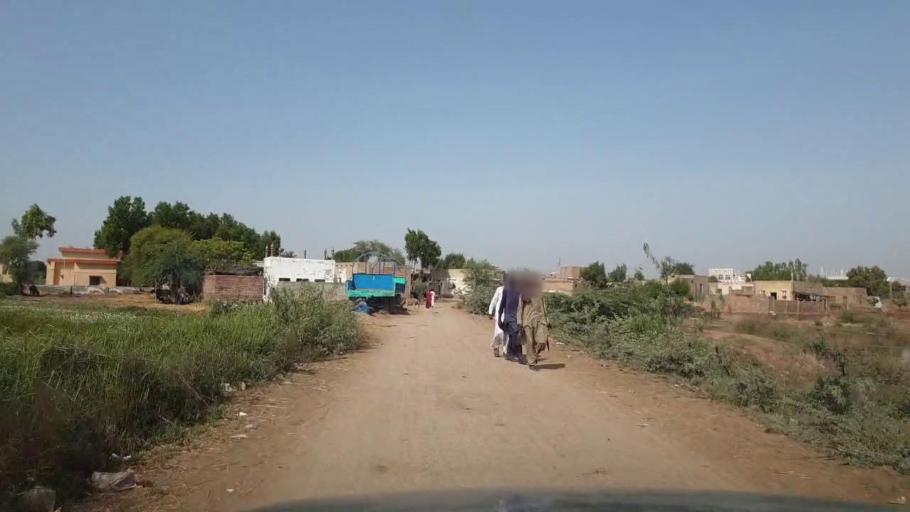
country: PK
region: Sindh
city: Tando Muhammad Khan
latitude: 25.1584
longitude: 68.3884
